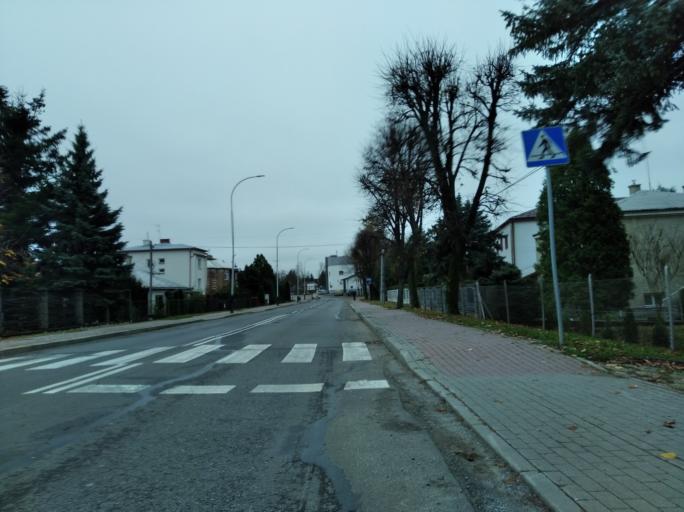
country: PL
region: Subcarpathian Voivodeship
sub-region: Krosno
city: Krosno
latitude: 49.6983
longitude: 21.7630
